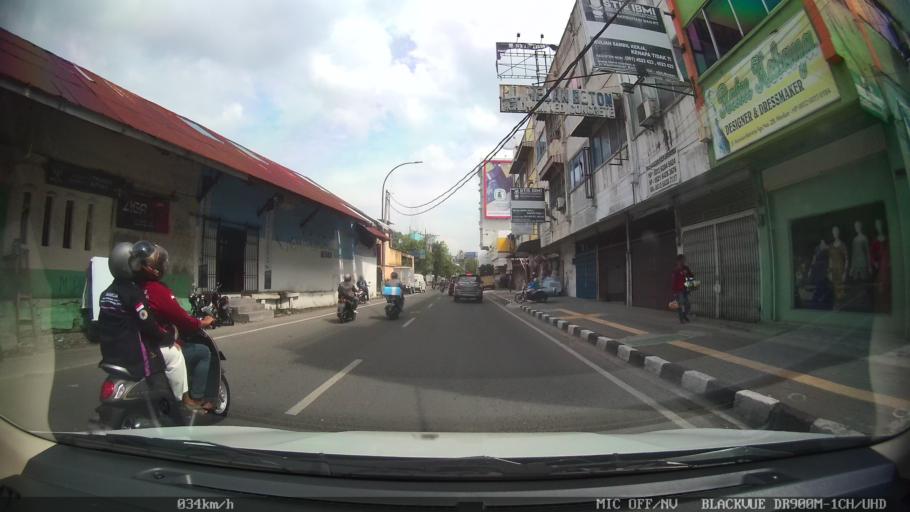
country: ID
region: North Sumatra
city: Medan
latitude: 3.5894
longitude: 98.6802
